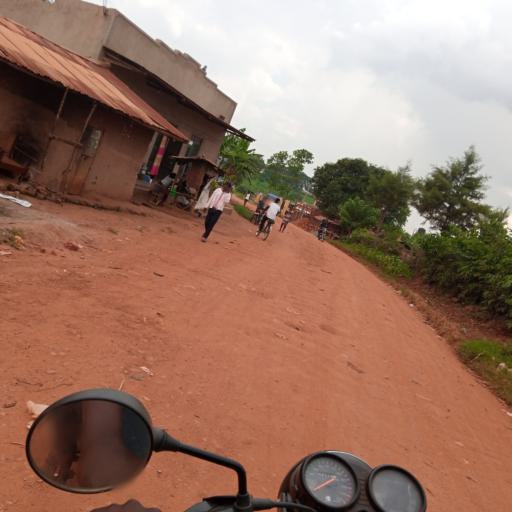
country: UG
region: Eastern Region
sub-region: Mbale District
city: Mbale
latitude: 1.1062
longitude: 34.1741
